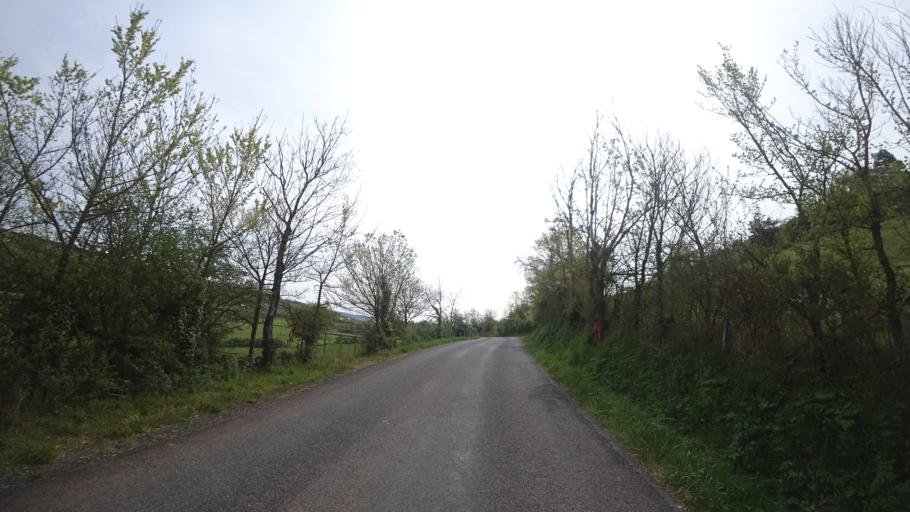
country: FR
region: Midi-Pyrenees
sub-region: Departement de l'Aveyron
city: Sebazac-Concoures
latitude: 44.3732
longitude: 2.6125
